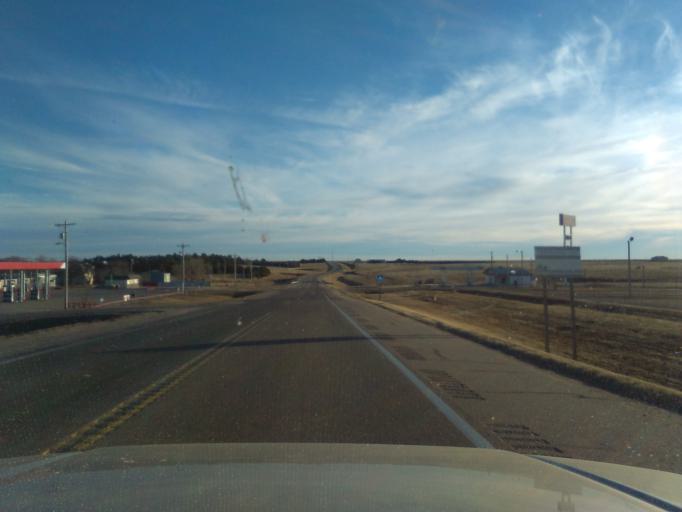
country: US
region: Kansas
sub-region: Logan County
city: Oakley
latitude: 39.1868
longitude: -100.8699
